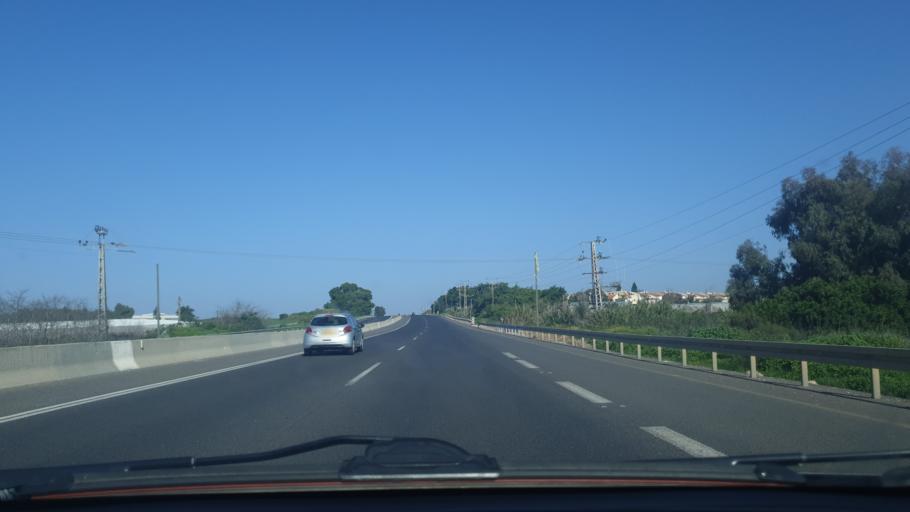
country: IL
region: Central District
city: Bet Dagan
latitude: 31.9912
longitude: 34.8284
